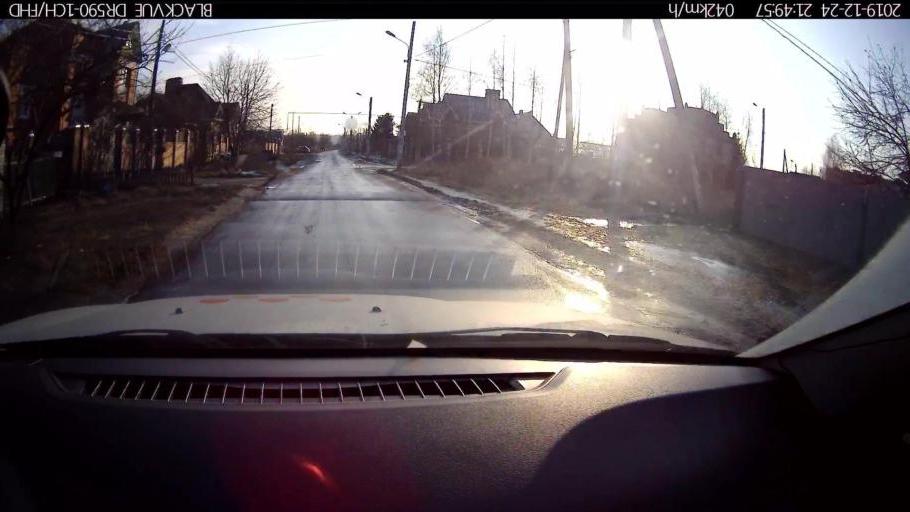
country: RU
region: Nizjnij Novgorod
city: Burevestnik
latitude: 56.2231
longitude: 43.8436
